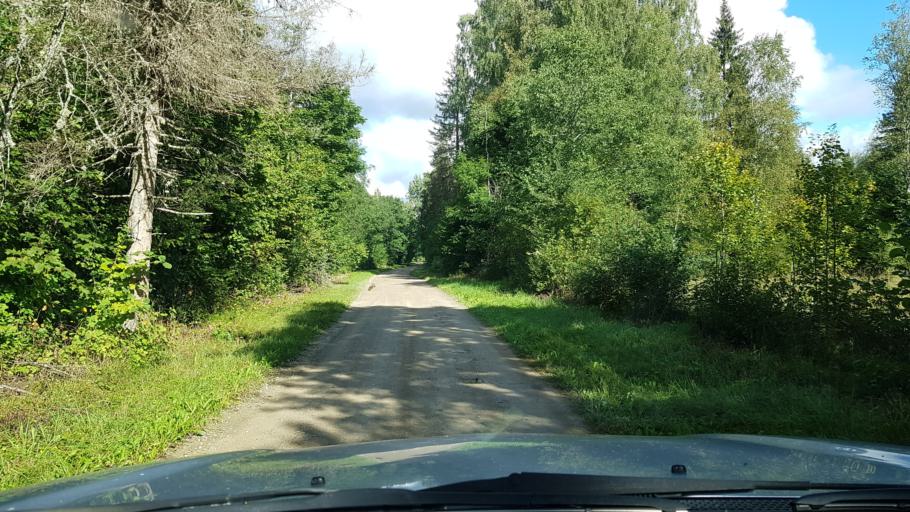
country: EE
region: Harju
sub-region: Raasiku vald
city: Arukula
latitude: 59.2584
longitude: 25.0984
